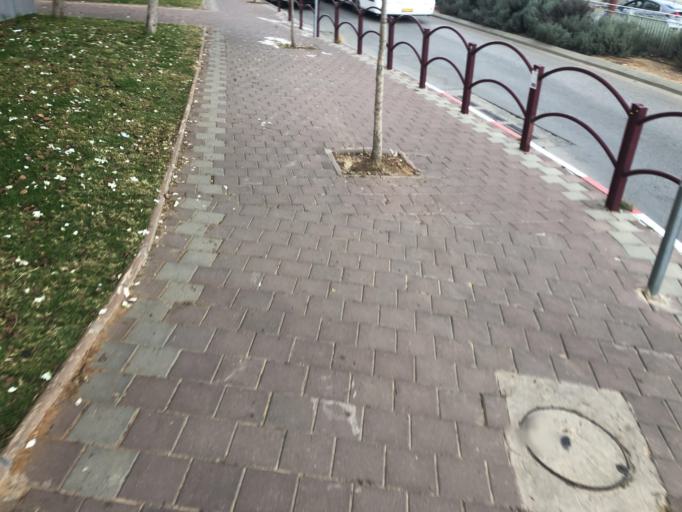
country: IL
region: Jerusalem
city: Modiin Ilit
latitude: 31.9377
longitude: 35.0470
